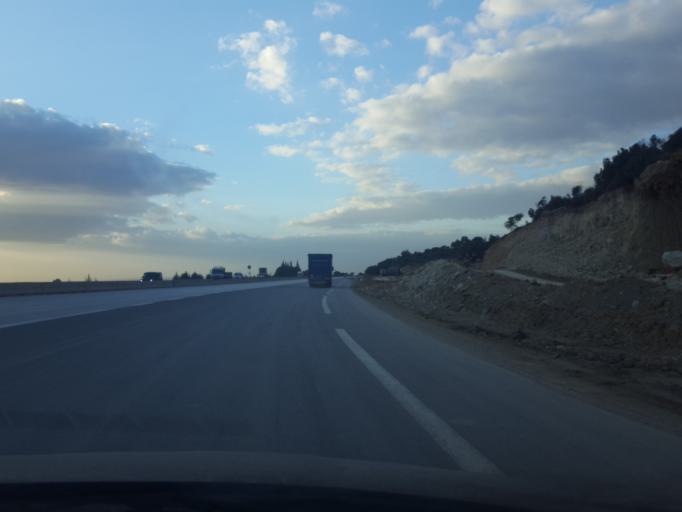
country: TN
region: Tunis
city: La Sebala du Mornag
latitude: 36.6469
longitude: 10.3617
